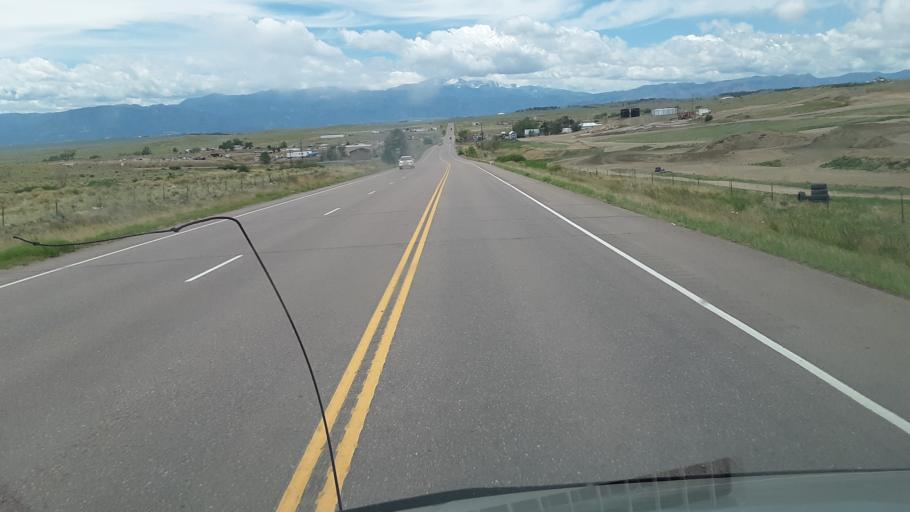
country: US
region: Colorado
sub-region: El Paso County
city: Cimarron Hills
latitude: 38.8386
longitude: -104.5864
